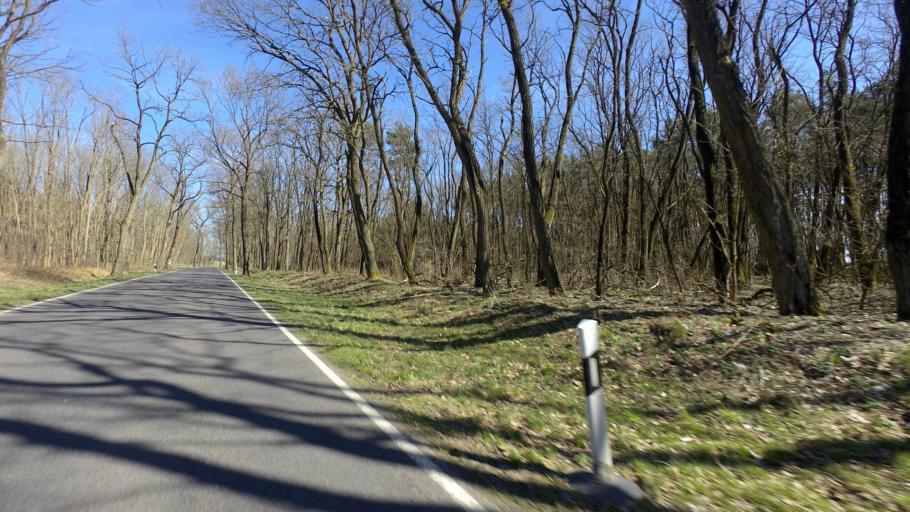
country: DE
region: Brandenburg
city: Munchehofe
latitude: 52.1568
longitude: 13.8623
